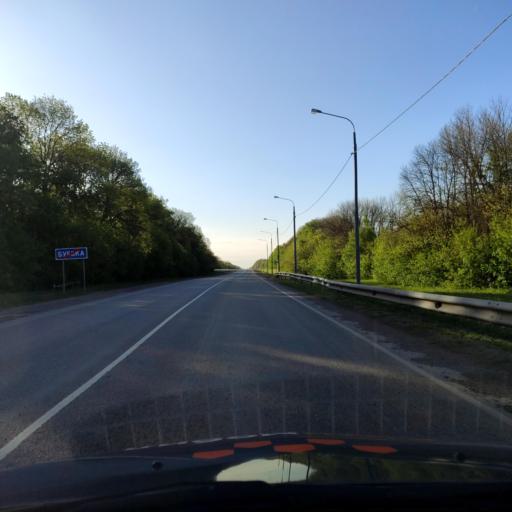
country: RU
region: Lipetsk
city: Yelets
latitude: 52.5800
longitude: 38.6368
